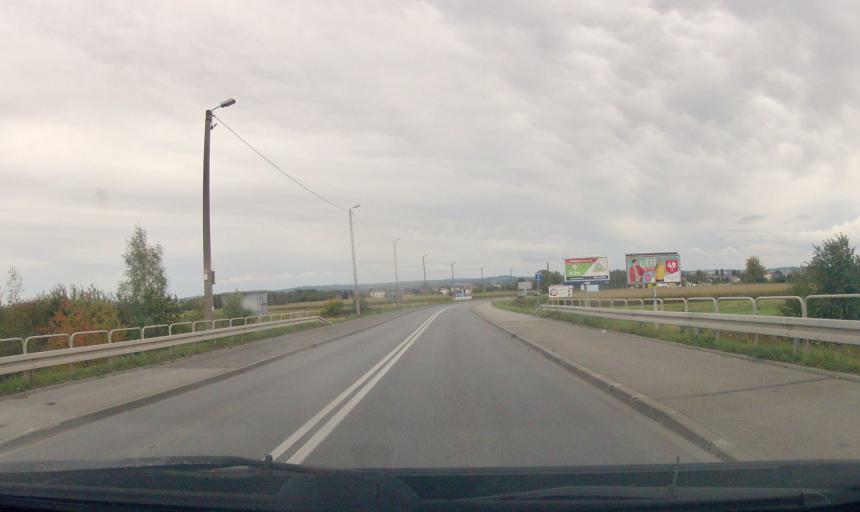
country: PL
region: Lesser Poland Voivodeship
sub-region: Powiat wielicki
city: Kokotow
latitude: 50.0499
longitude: 20.0498
